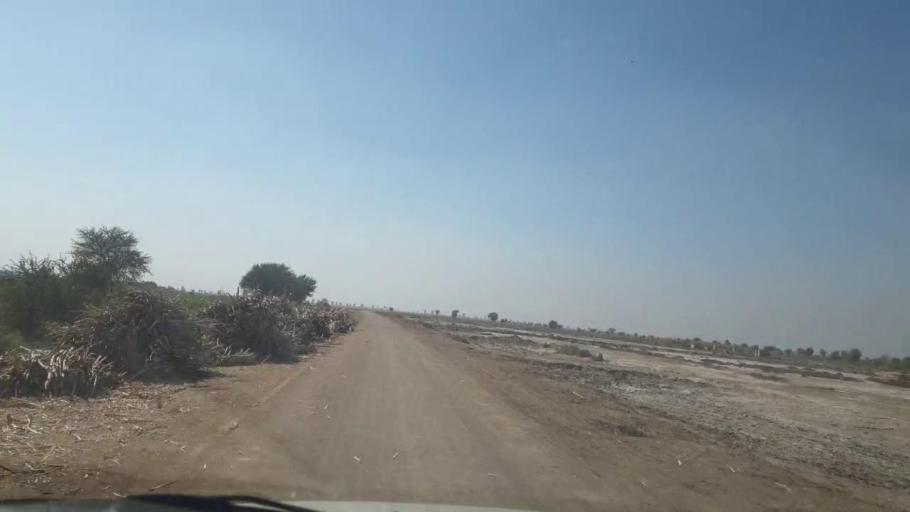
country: PK
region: Sindh
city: Mirpur Khas
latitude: 25.4706
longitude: 69.1708
